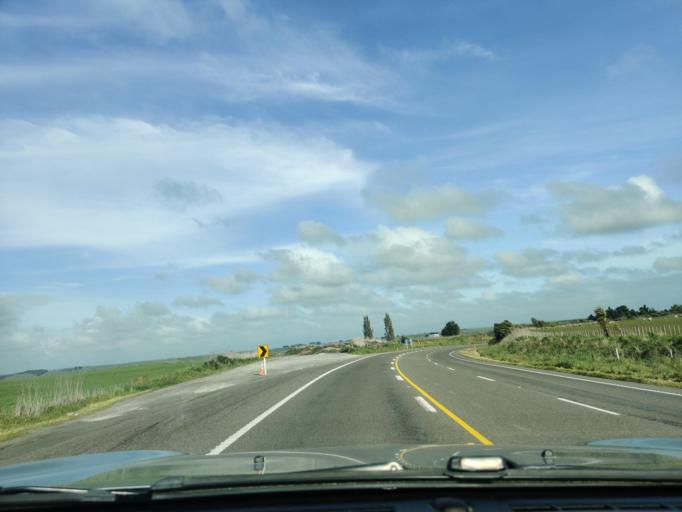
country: NZ
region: Manawatu-Wanganui
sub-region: Wanganui District
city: Wanganui
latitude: -39.9931
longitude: 175.1673
